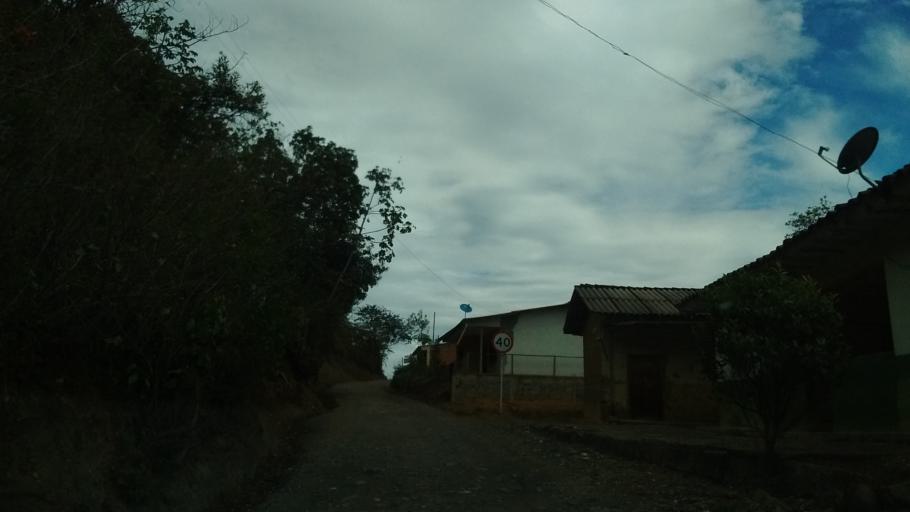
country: CO
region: Cauca
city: Almaguer
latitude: 1.8478
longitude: -76.9015
